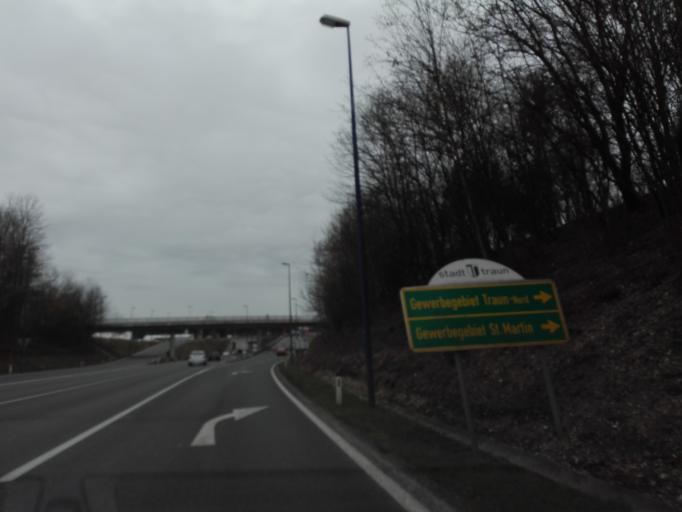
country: AT
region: Upper Austria
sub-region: Politischer Bezirk Linz-Land
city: Traun
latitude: 48.2283
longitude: 14.2227
